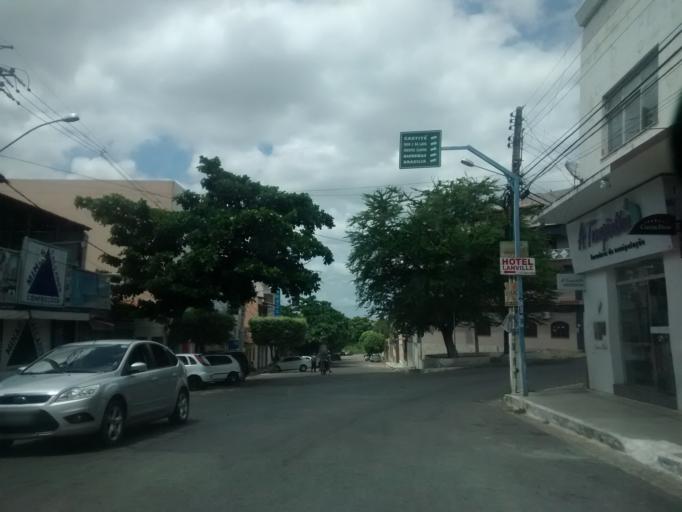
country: BR
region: Bahia
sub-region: Brumado
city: Brumado
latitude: -14.2076
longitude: -41.6661
